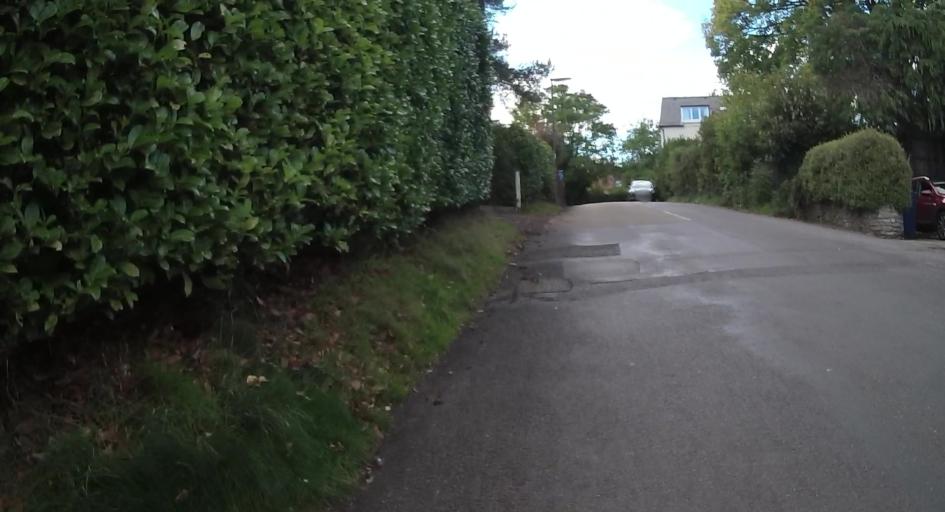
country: GB
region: England
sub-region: Surrey
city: Farnham
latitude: 51.1958
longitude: -0.8089
